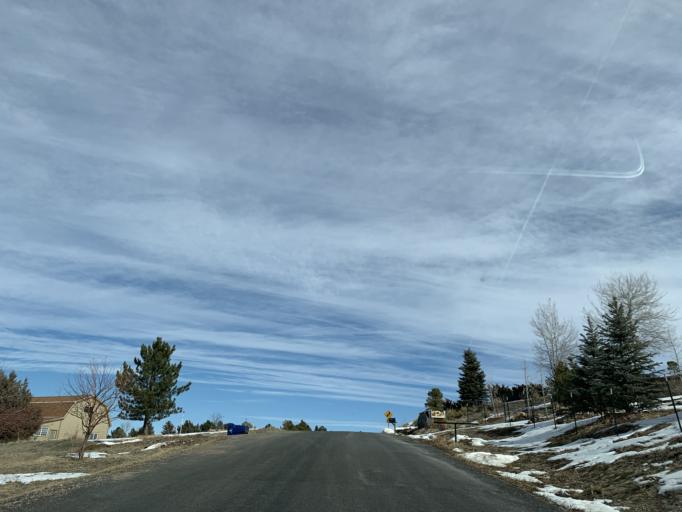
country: US
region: Colorado
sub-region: Douglas County
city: Carriage Club
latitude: 39.5174
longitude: -104.8991
